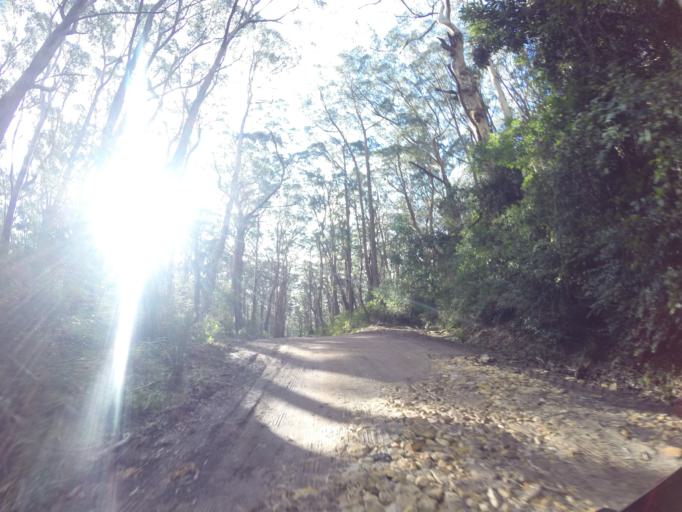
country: AU
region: New South Wales
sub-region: Wollongong
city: Cordeaux Heights
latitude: -34.4187
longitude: 150.7841
